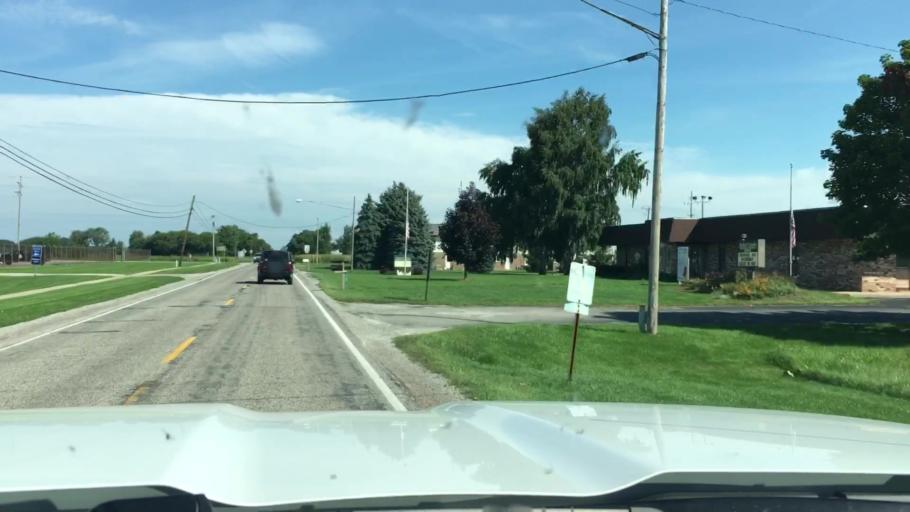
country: US
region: Michigan
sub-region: Saginaw County
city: Hemlock
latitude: 43.4235
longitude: -84.2298
